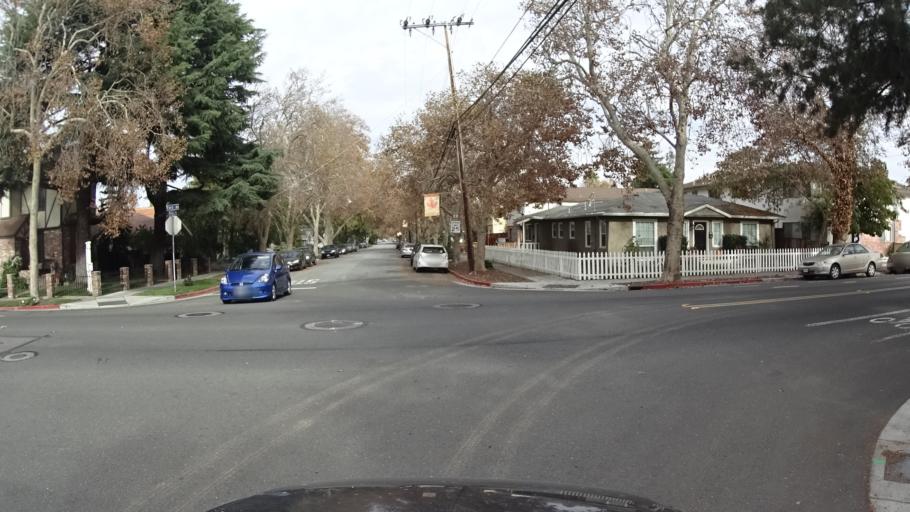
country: US
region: California
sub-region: Santa Clara County
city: Burbank
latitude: 37.3380
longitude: -121.9291
